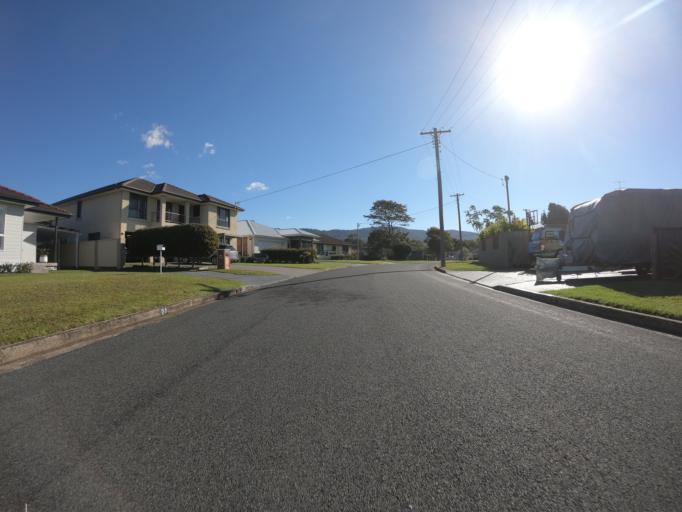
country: AU
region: New South Wales
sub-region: Wollongong
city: Bulli
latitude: -34.3552
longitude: 150.9159
